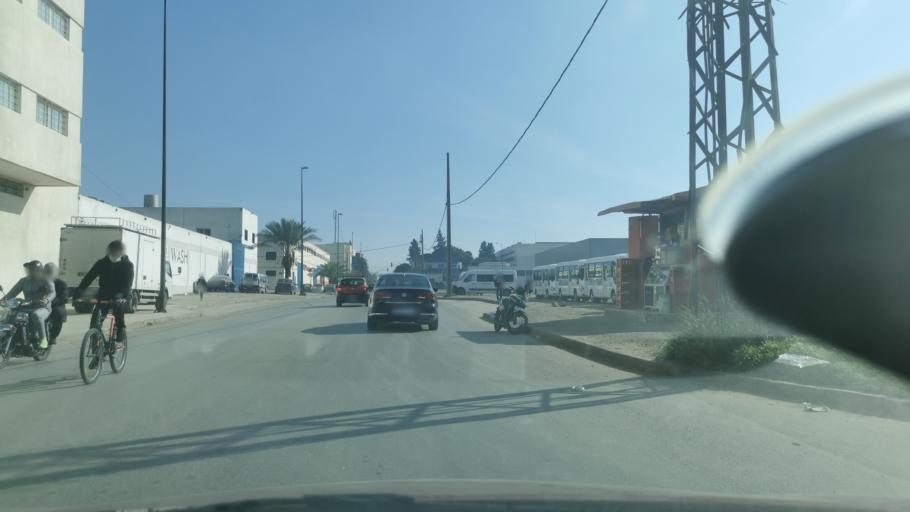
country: MA
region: Fes-Boulemane
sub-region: Fes
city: Fes
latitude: 34.0267
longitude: -4.9781
